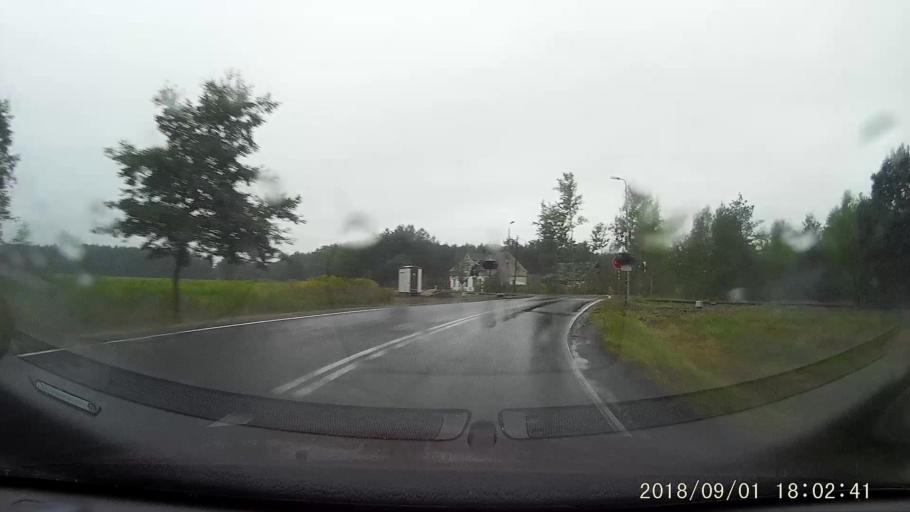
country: PL
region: Lubusz
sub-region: Powiat zaganski
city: Gozdnica
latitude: 51.3845
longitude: 15.1747
